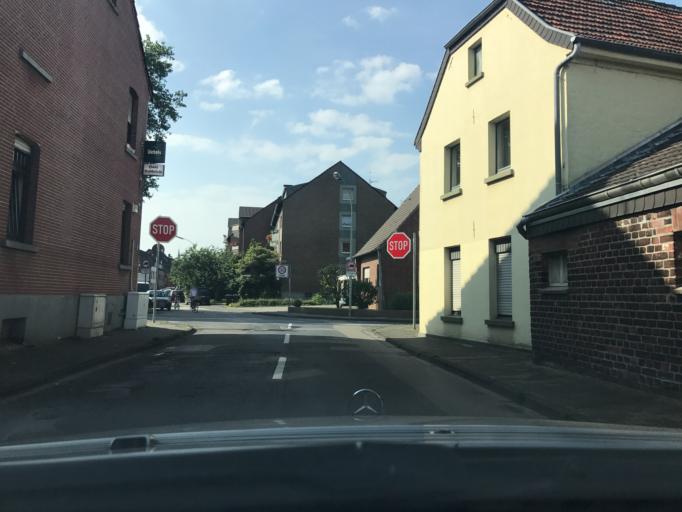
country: DE
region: North Rhine-Westphalia
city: Tonisvorst
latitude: 51.3676
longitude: 6.5180
